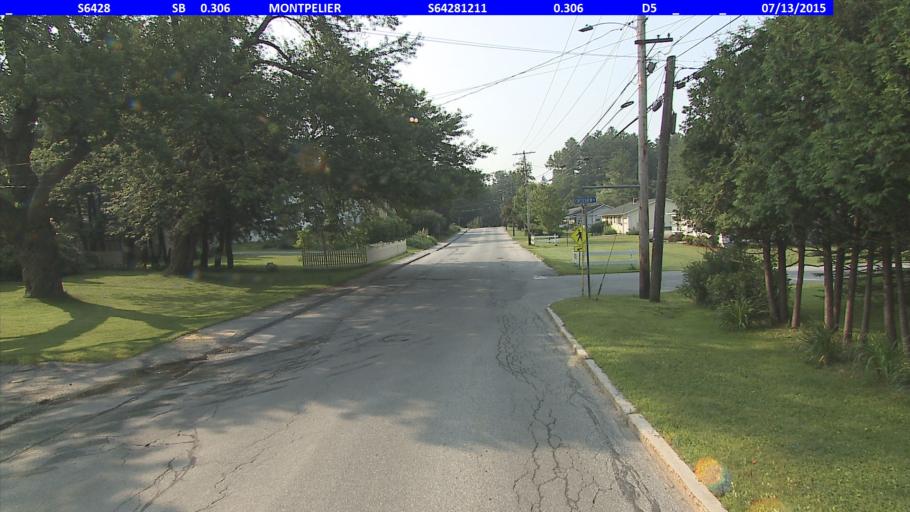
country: US
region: Vermont
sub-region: Washington County
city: Montpelier
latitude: 44.2673
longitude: -72.5874
